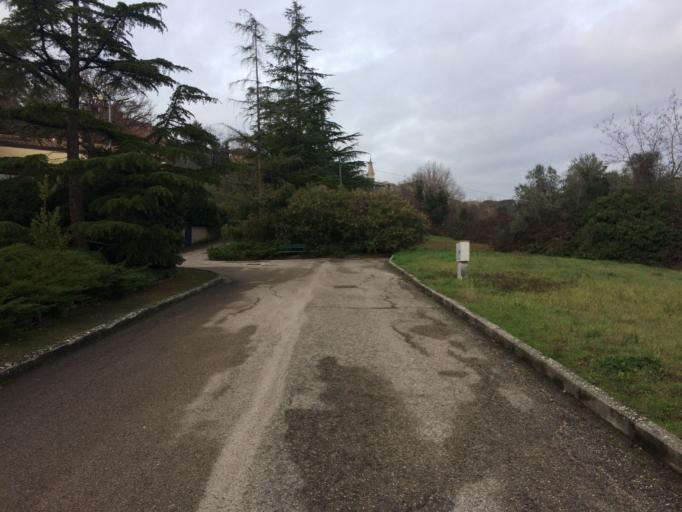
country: IT
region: Umbria
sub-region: Provincia di Perugia
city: Perugia
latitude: 43.0976
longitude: 12.4021
